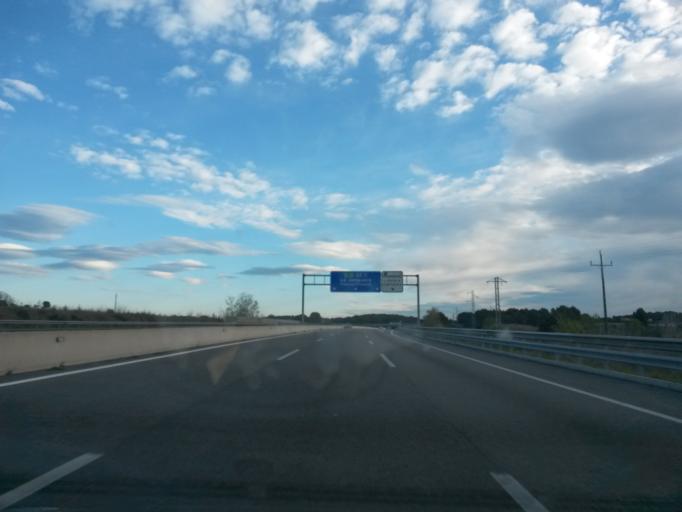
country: ES
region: Catalonia
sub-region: Provincia de Girona
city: Vilademuls
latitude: 42.1253
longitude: 2.9120
